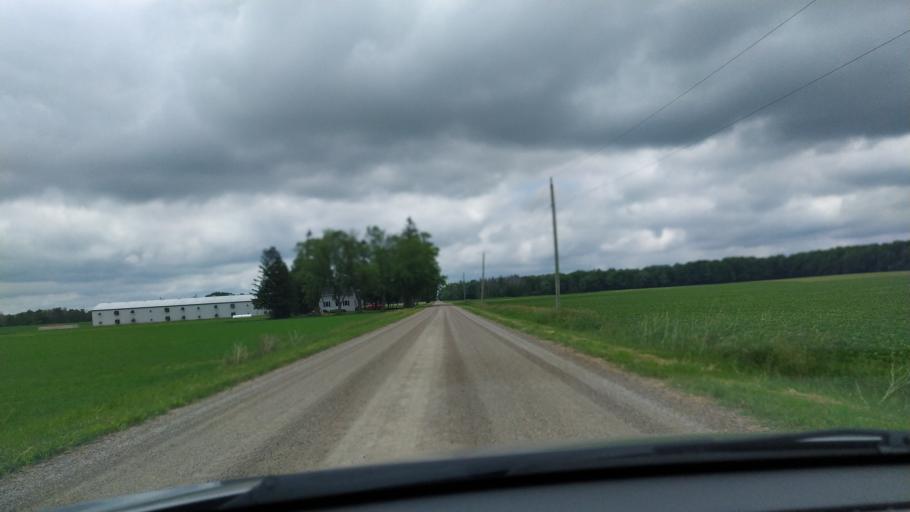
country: CA
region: Ontario
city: Stratford
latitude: 43.4087
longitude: -80.8880
